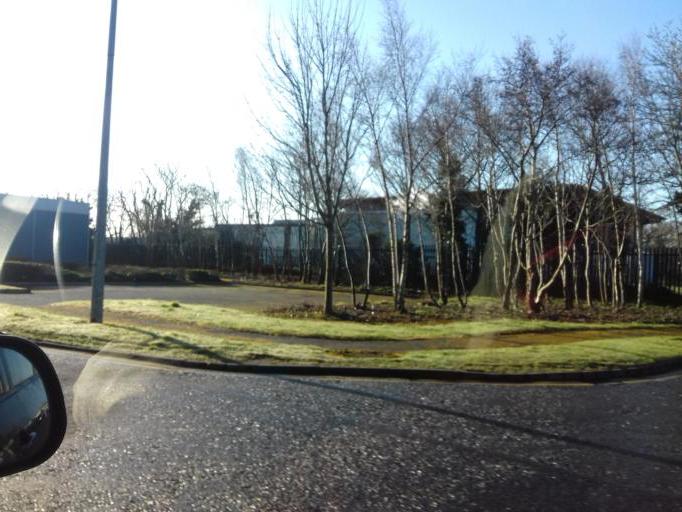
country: IE
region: Leinster
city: Beaumont
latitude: 53.4093
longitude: -6.2492
